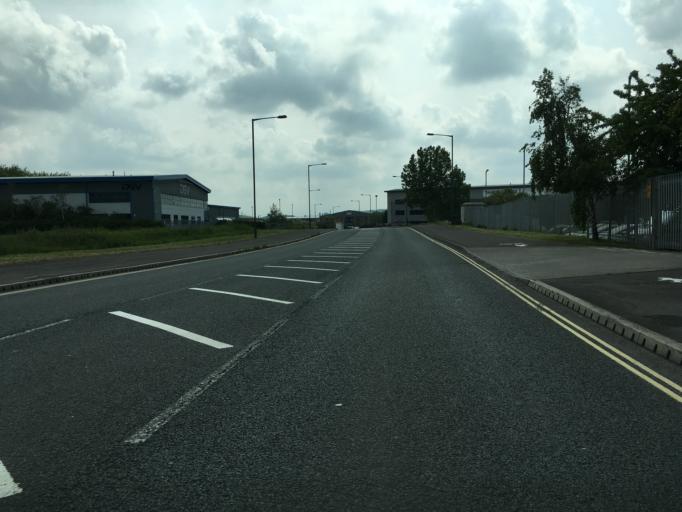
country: GB
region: England
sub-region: South Gloucestershire
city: Severn Beach
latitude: 51.5188
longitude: -2.6745
